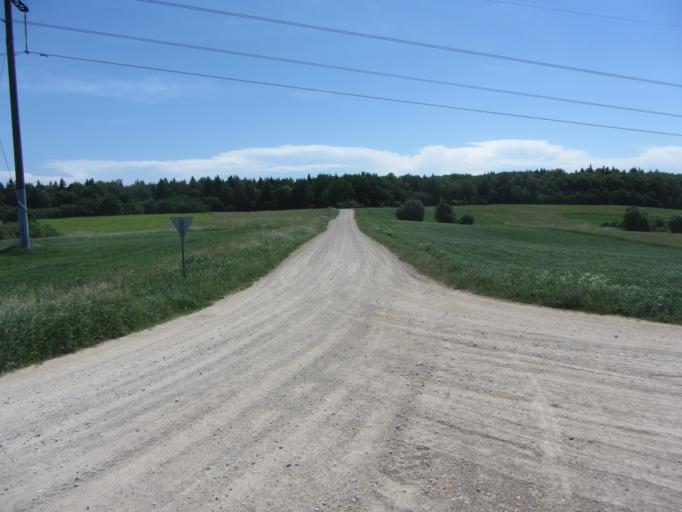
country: LT
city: Jieznas
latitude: 54.5509
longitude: 24.3125
